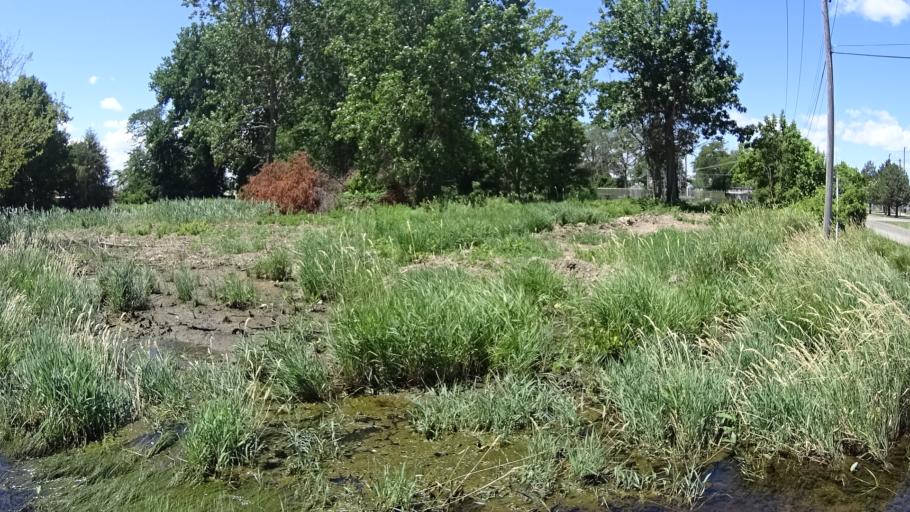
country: US
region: Ohio
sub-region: Erie County
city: Sandusky
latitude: 41.4497
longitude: -82.6707
